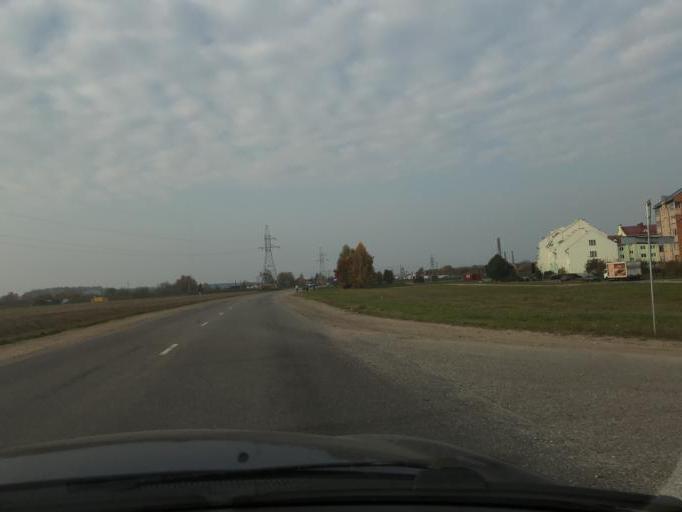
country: BY
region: Grodnenskaya
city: Lida
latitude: 53.8609
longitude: 25.2866
